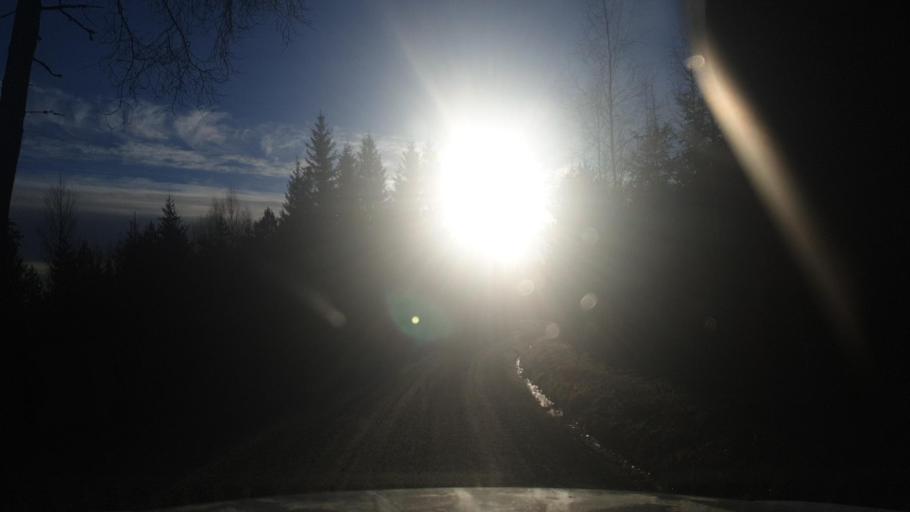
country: SE
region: Vaermland
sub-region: Karlstads Kommun
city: Edsvalla
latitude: 59.5971
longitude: 13.0708
